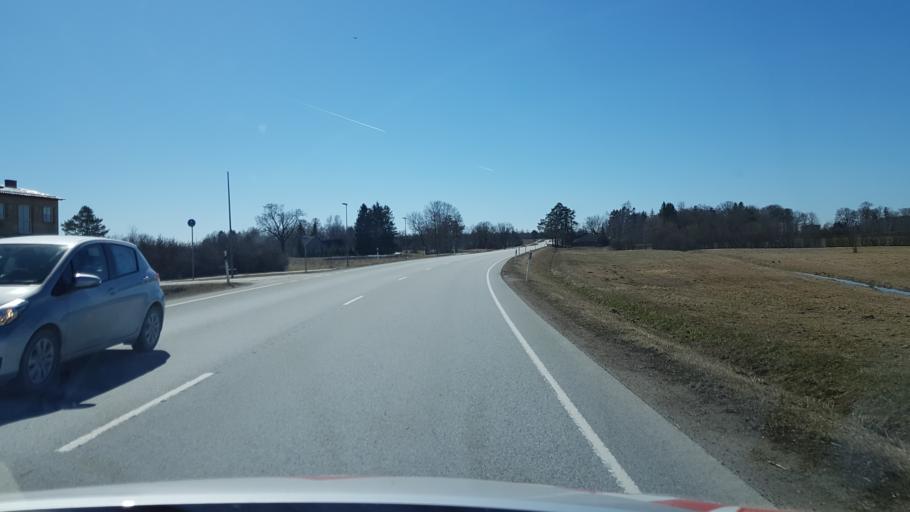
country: EE
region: Laeaene-Virumaa
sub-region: Rakvere linn
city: Rakvere
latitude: 59.4214
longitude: 26.3545
